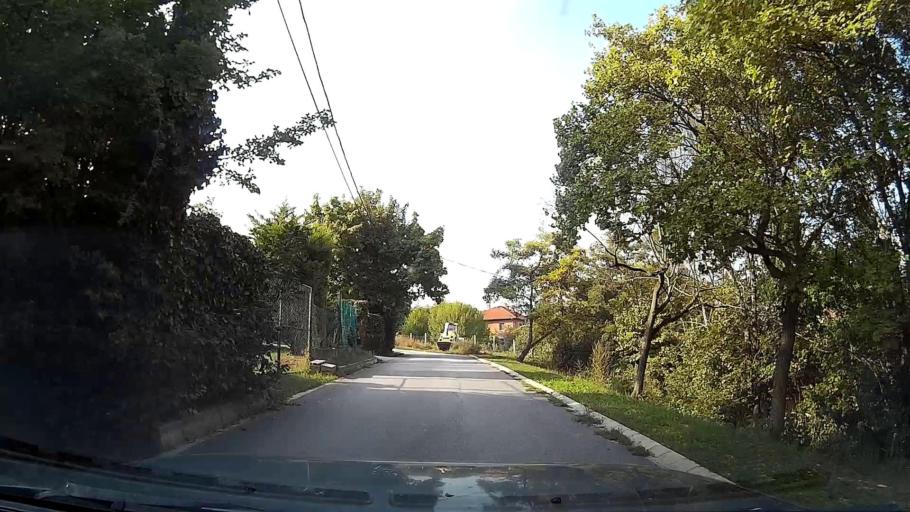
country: HU
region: Pest
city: Nagykovacsi
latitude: 47.6548
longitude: 19.0157
